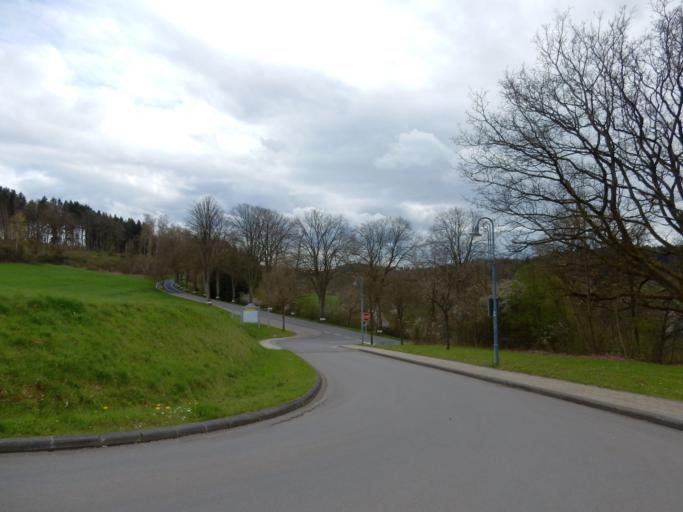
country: LU
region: Luxembourg
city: Eischen
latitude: 49.6808
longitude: 5.8816
